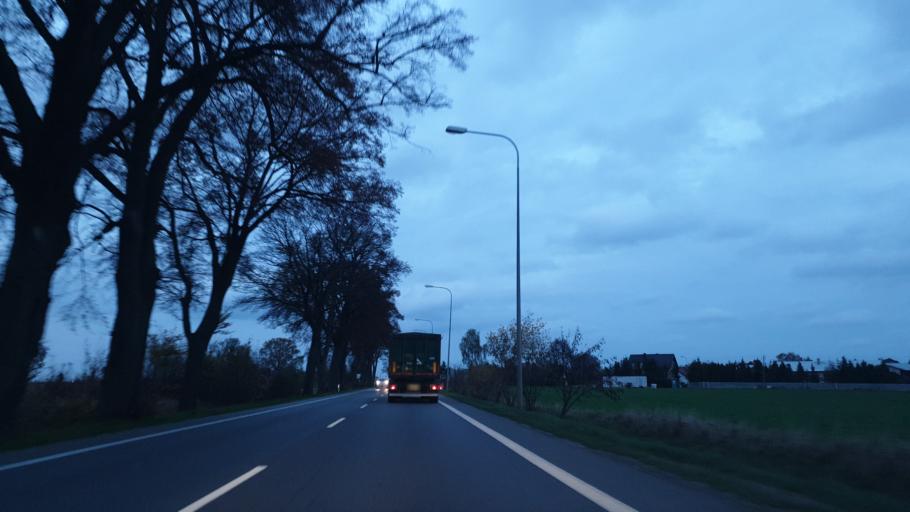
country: PL
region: Pomeranian Voivodeship
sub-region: Powiat wejherowski
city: Rekowo Dolne
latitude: 54.6445
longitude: 18.3507
